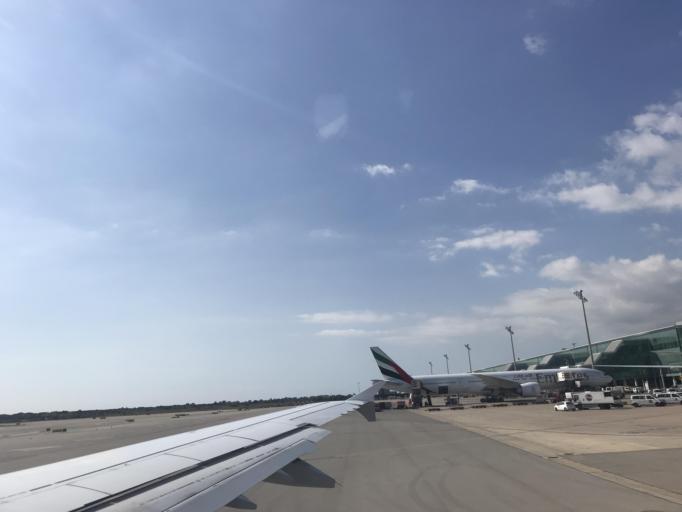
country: ES
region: Catalonia
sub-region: Provincia de Barcelona
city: El Prat de Llobregat
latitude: 41.2873
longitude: 2.0792
